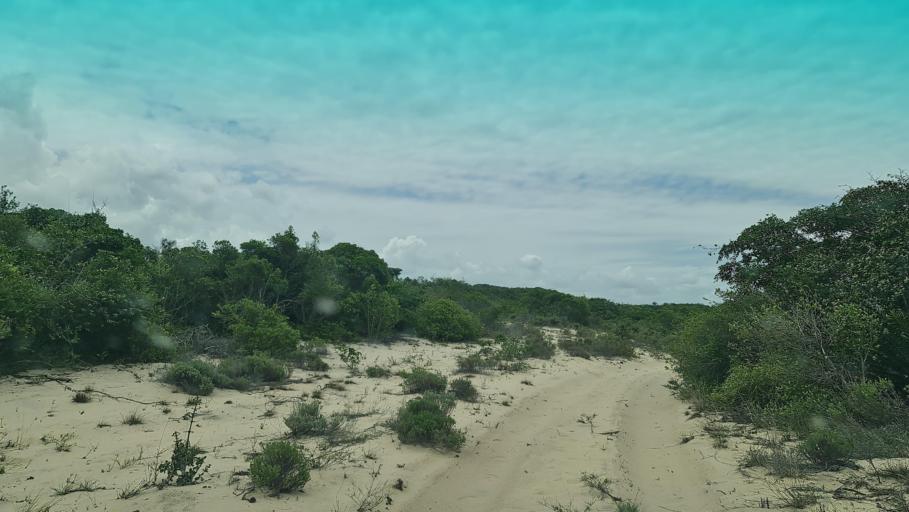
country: MZ
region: Maputo
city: Manhica
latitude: -25.6342
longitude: 32.7857
